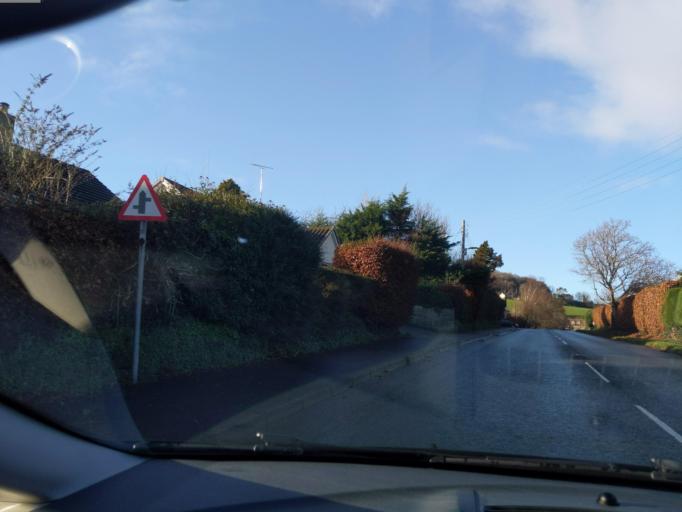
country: GB
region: England
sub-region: Devon
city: Okehampton
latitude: 50.7406
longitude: -4.0082
